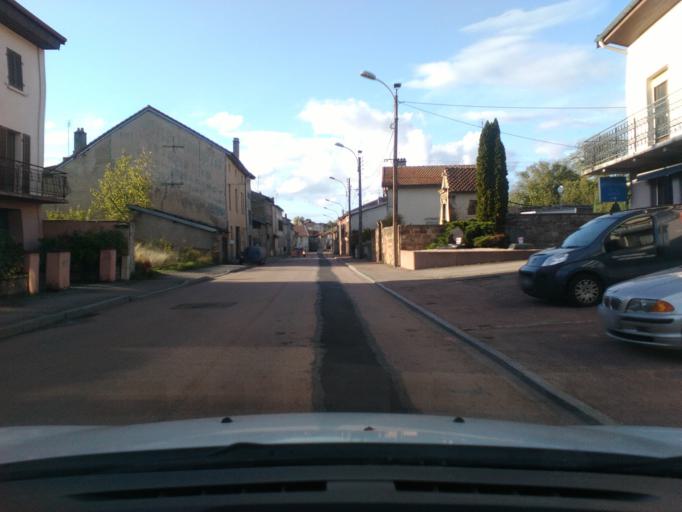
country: FR
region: Lorraine
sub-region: Departement des Vosges
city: Rambervillers
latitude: 48.3444
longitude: 6.6408
